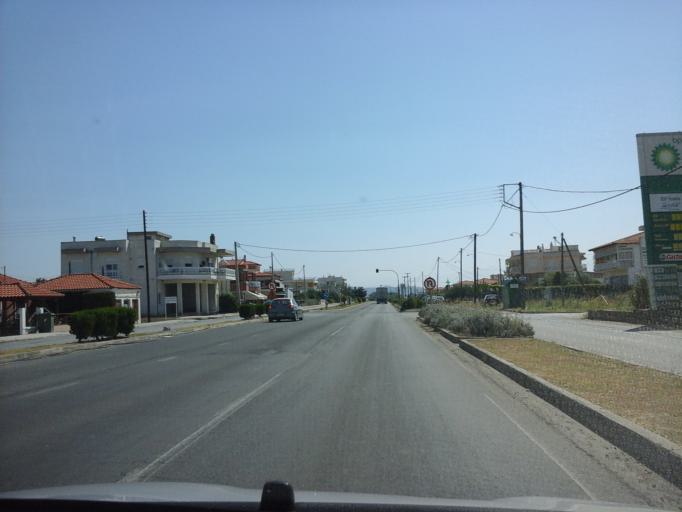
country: GR
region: East Macedonia and Thrace
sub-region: Nomos Evrou
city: Alexandroupoli
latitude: 40.8558
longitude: 25.9325
